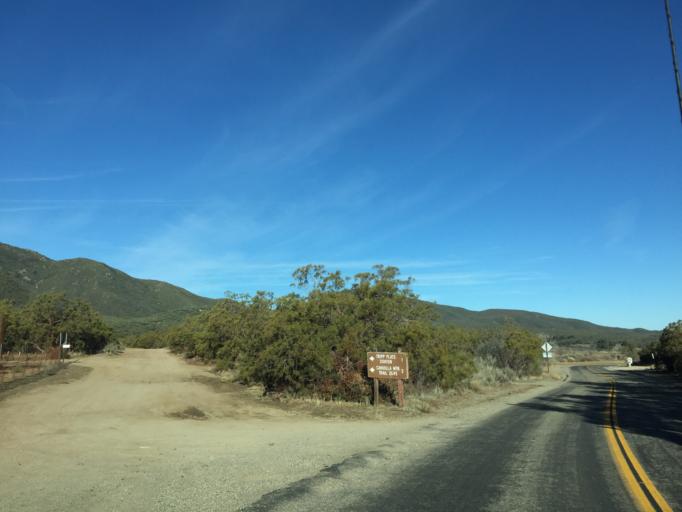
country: US
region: California
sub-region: Riverside County
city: Anza
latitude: 33.5871
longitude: -116.7530
